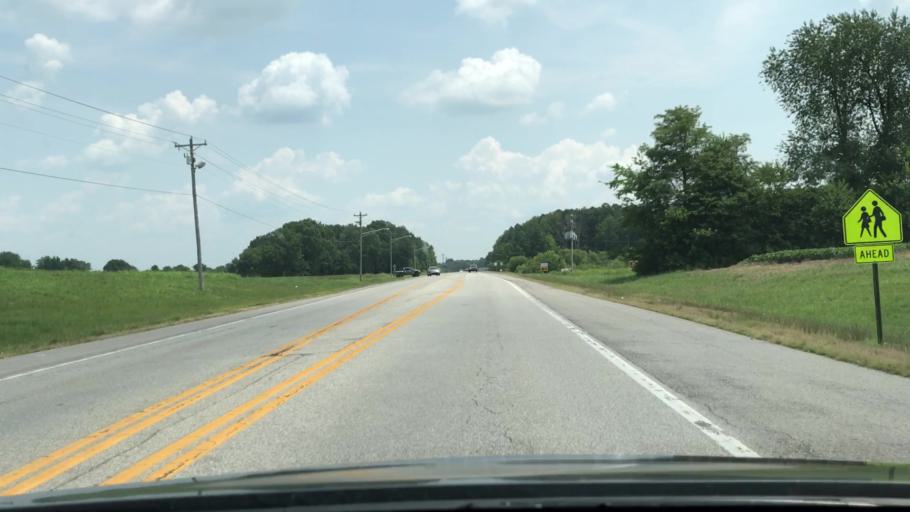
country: US
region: Tennessee
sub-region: Sumner County
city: Portland
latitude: 36.5781
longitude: -86.5342
